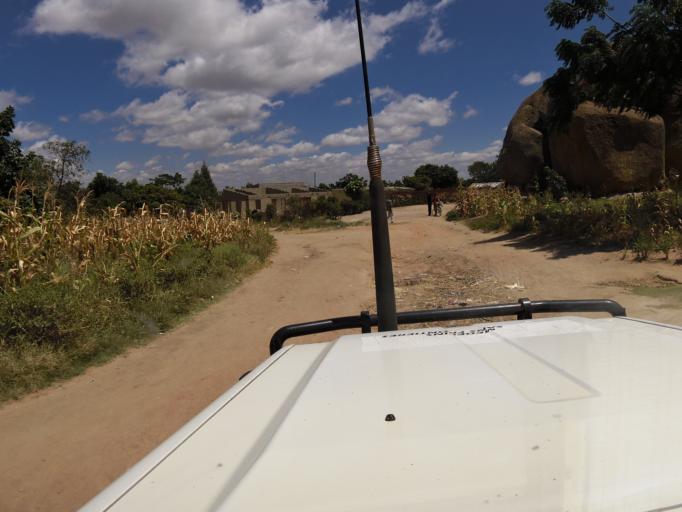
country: ZW
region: Harare
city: Epworth
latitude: -17.9039
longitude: 31.1552
